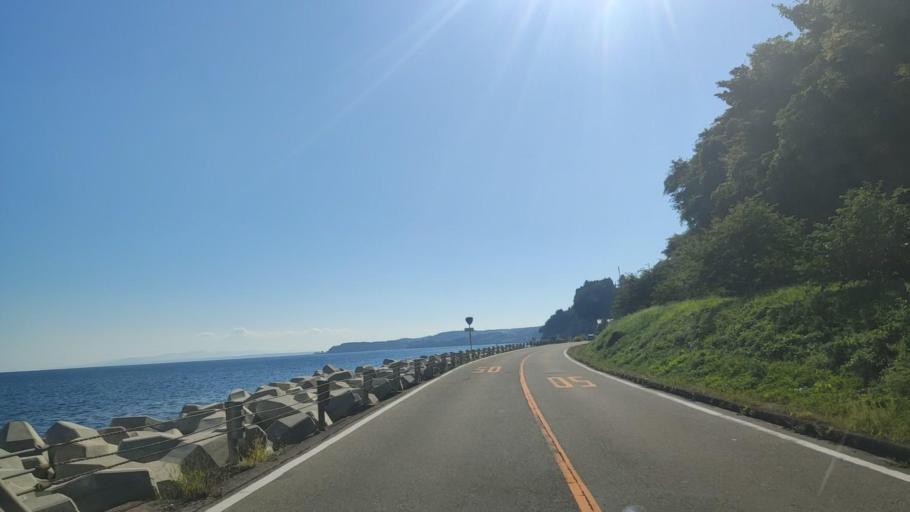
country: JP
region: Ishikawa
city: Nanao
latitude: 37.2865
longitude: 137.1145
